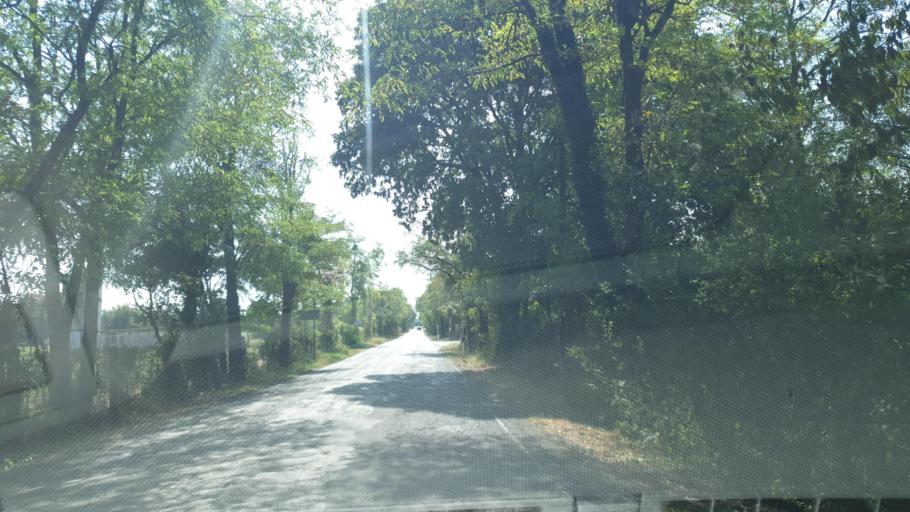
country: IT
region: Lombardy
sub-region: Provincia di Brescia
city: Carzago Riviera
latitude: 45.5053
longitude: 10.4642
